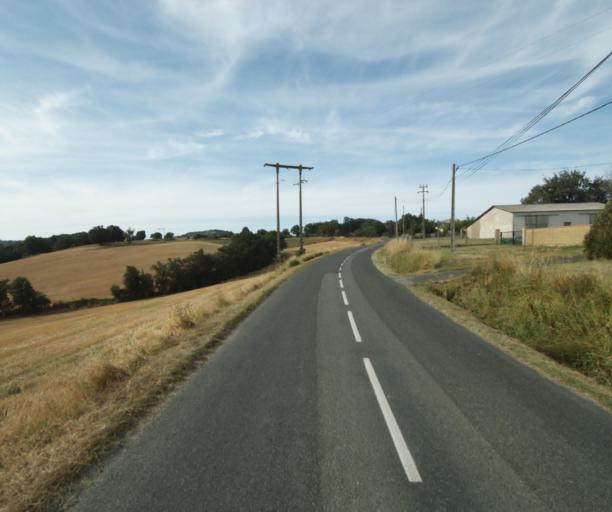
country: FR
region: Midi-Pyrenees
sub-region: Departement du Tarn
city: Puylaurens
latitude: 43.5410
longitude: 2.0592
